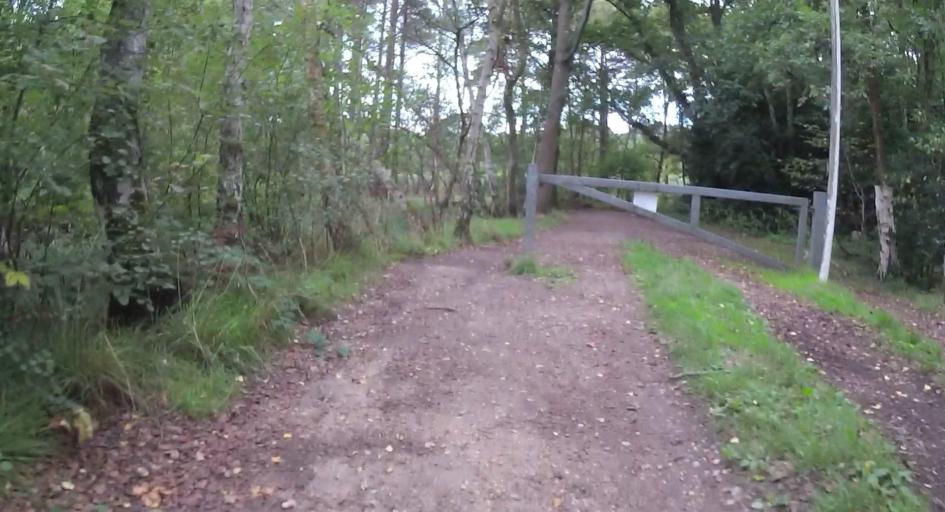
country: GB
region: England
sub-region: Surrey
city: Windlesham
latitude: 51.3388
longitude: -0.6622
